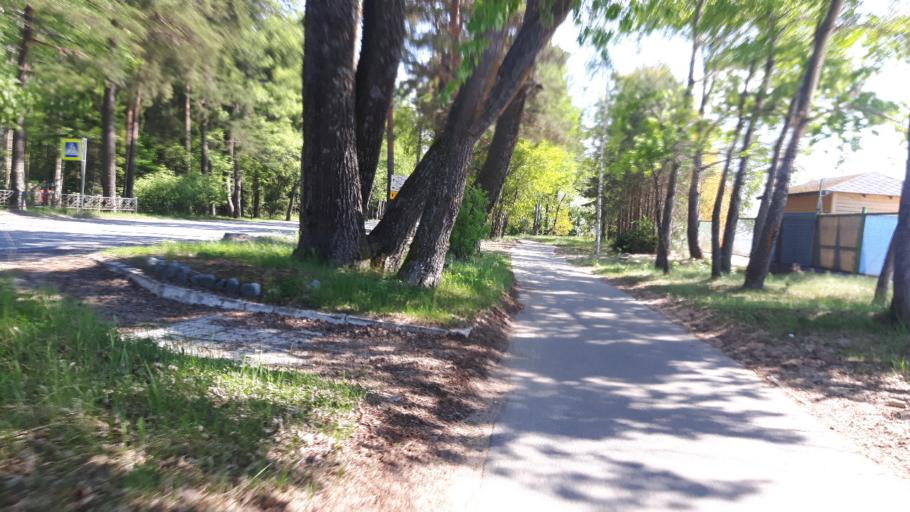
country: RU
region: St.-Petersburg
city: Komarovo
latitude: 60.1727
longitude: 29.8058
